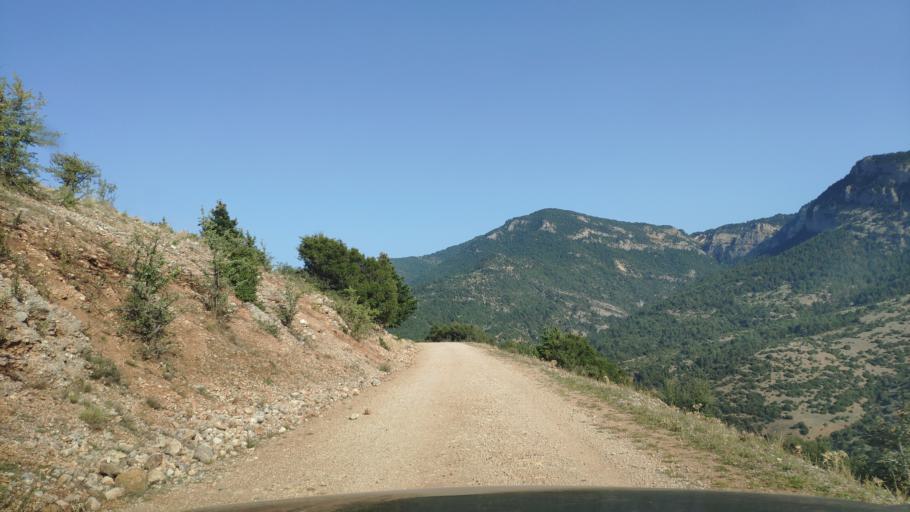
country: GR
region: West Greece
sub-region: Nomos Achaias
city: Aiyira
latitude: 37.9852
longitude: 22.3480
